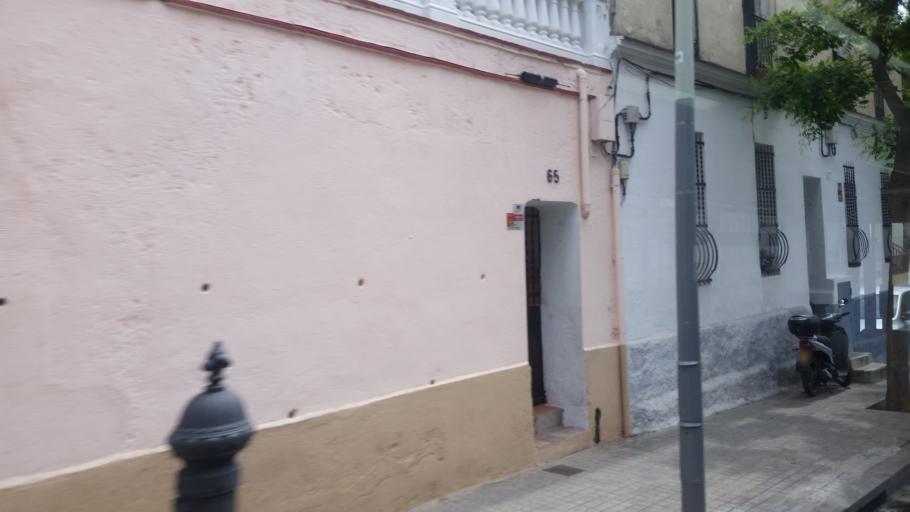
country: ES
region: Catalonia
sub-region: Provincia de Barcelona
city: Horta-Guinardo
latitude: 41.4206
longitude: 2.1613
